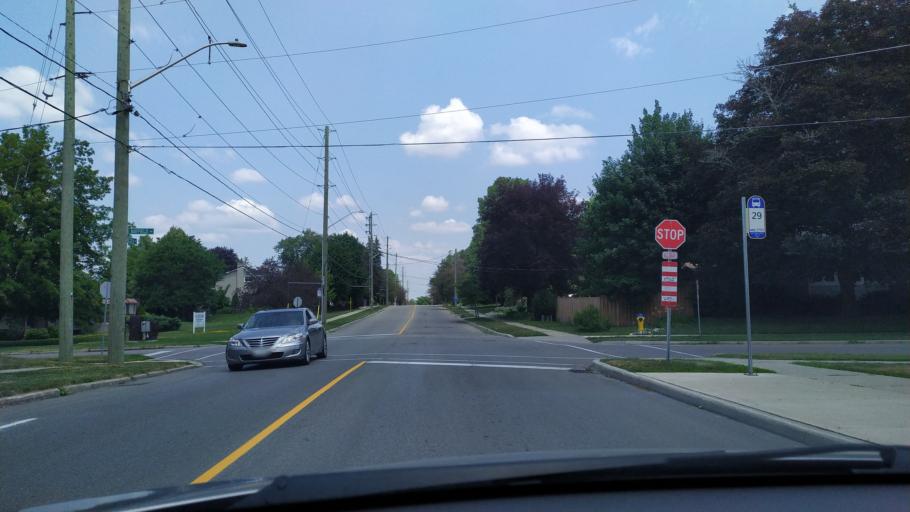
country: CA
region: Ontario
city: Waterloo
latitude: 43.4793
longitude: -80.5077
